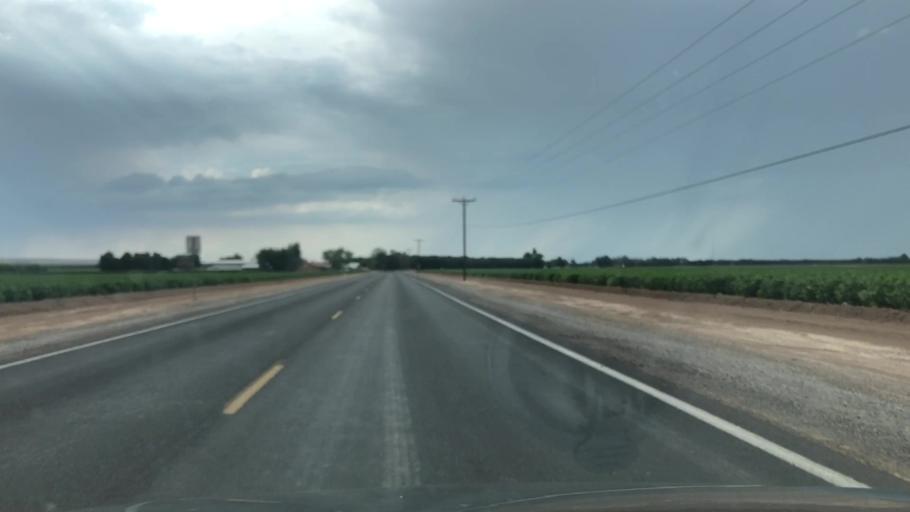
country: US
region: New Mexico
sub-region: Dona Ana County
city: La Union
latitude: 31.9656
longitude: -106.6490
